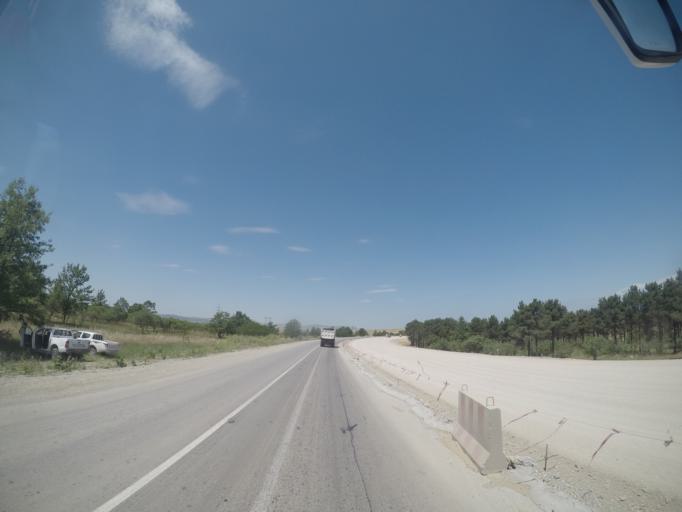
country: AZ
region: Qobustan
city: Qobustan
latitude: 40.5279
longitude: 48.7933
